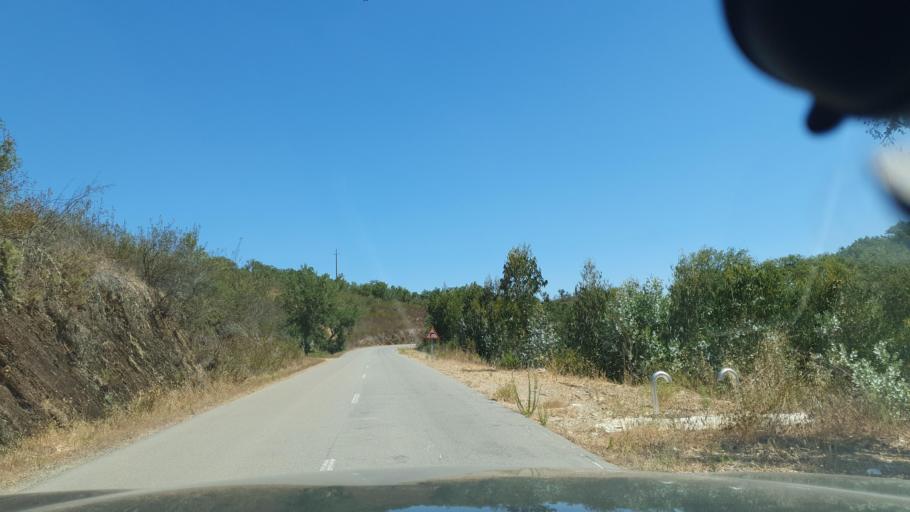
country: PT
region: Beja
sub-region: Odemira
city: Odemira
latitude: 37.5342
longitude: -8.4703
